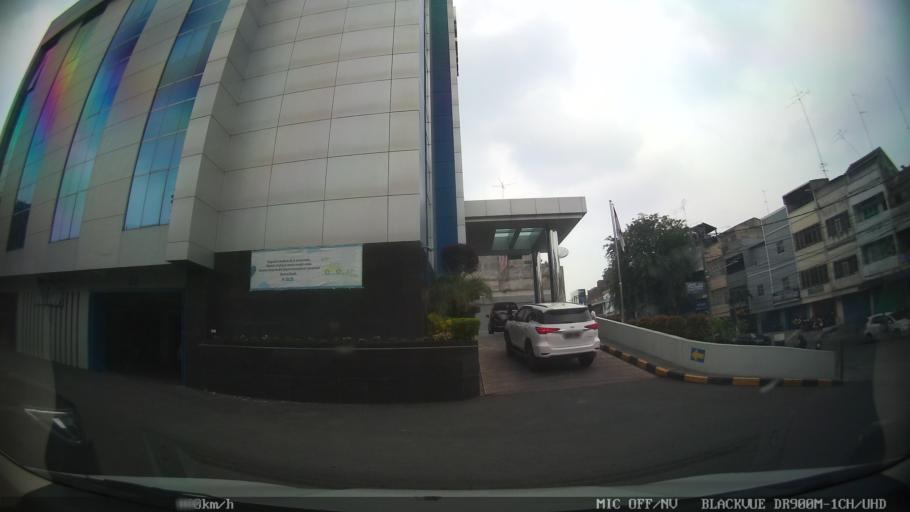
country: ID
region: North Sumatra
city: Medan
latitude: 3.5863
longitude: 98.6953
